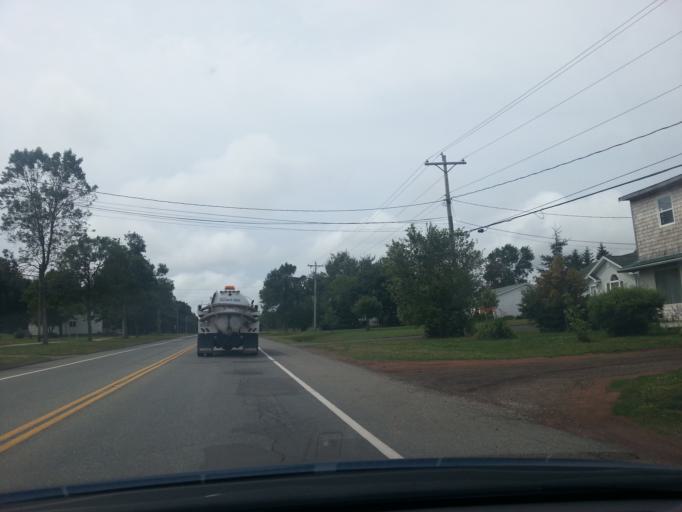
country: CA
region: Prince Edward Island
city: Charlottetown
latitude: 46.2848
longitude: -63.0942
